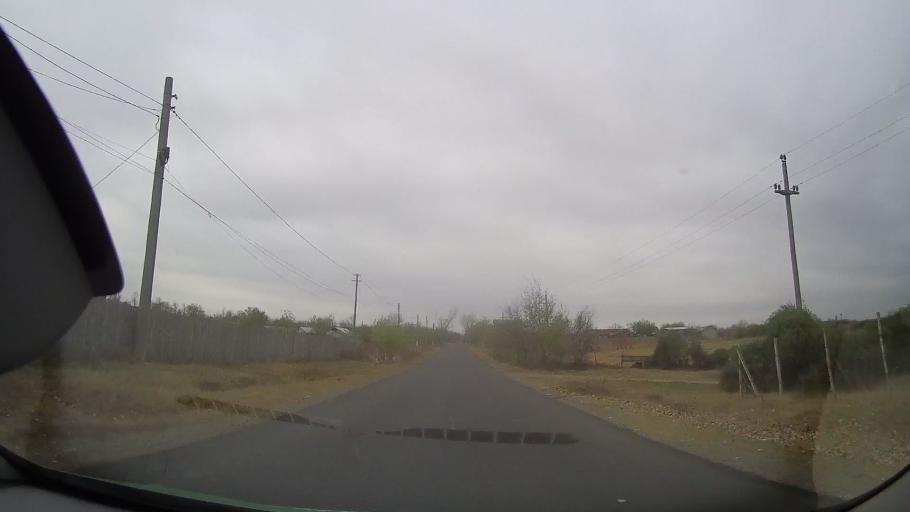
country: RO
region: Braila
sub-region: Comuna Ciresu
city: Ciresu
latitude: 44.9395
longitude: 27.3725
